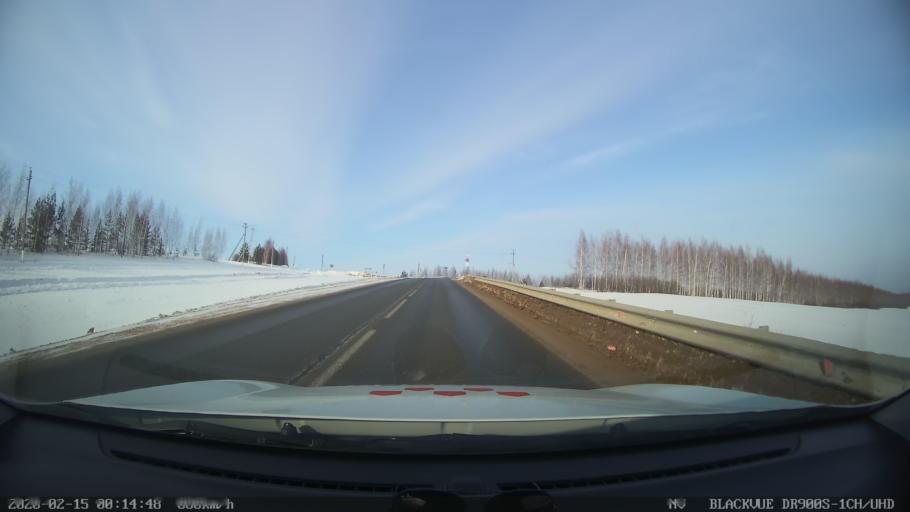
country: RU
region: Tatarstan
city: Stolbishchi
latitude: 55.4903
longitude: 49.0047
